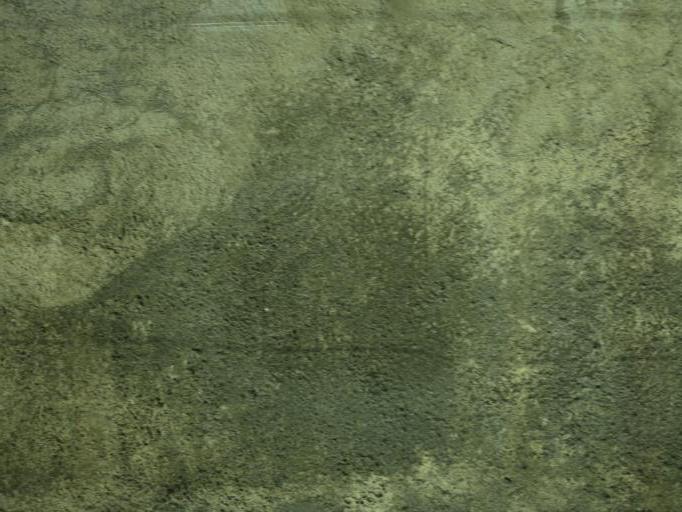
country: MA
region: Rabat-Sale-Zemmour-Zaer
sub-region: Rabat
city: Rabat
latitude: 34.0077
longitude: -6.8486
